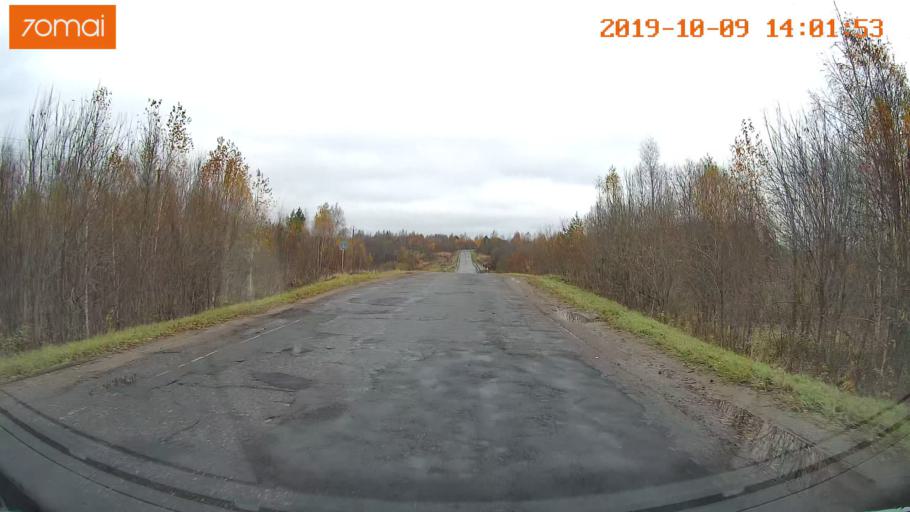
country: RU
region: Kostroma
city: Buy
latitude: 58.4462
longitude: 41.3509
